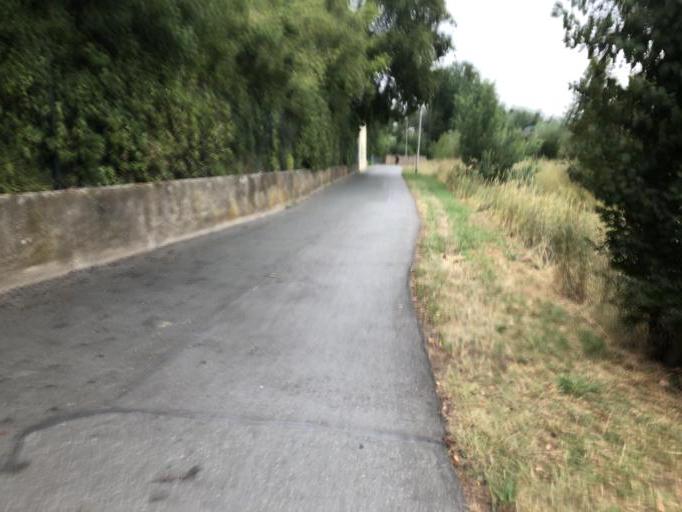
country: DE
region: Bavaria
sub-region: Regierungsbezirk Mittelfranken
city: Furth
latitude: 49.5090
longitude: 10.9748
